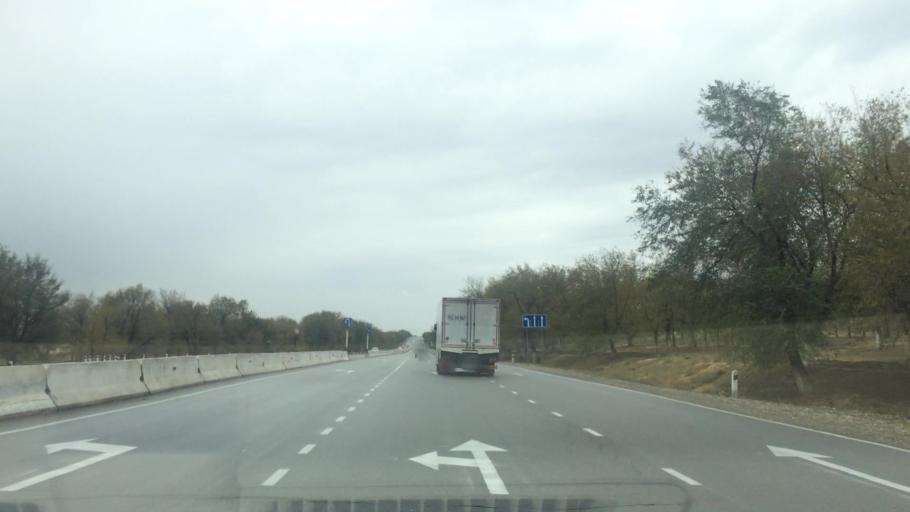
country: UZ
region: Samarqand
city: Bulung'ur
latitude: 39.9003
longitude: 67.5009
